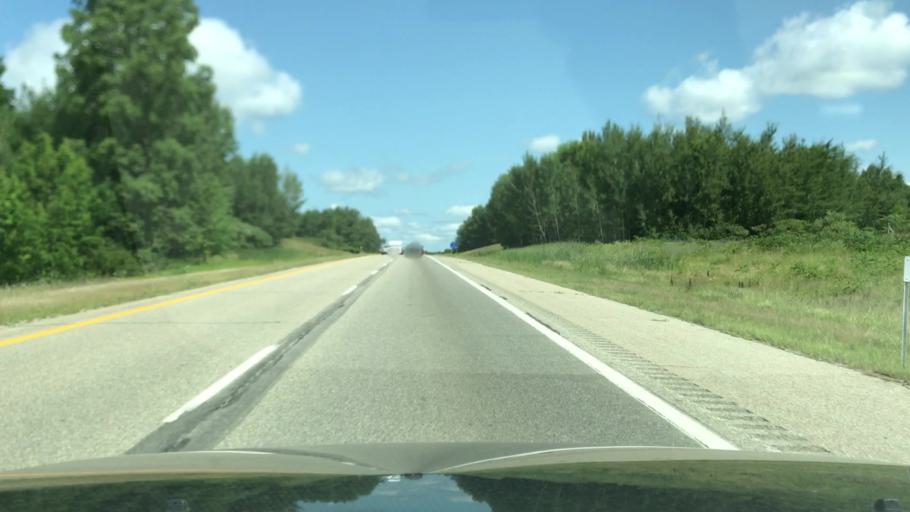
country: US
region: Michigan
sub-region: Mecosta County
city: Big Rapids
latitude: 43.7224
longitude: -85.5315
